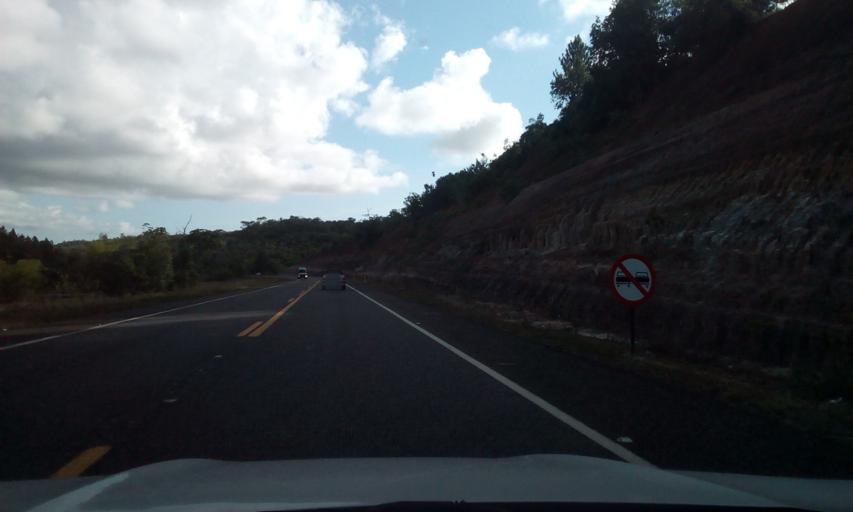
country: BR
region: Bahia
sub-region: Conde
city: Conde
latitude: -12.0751
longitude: -37.7532
